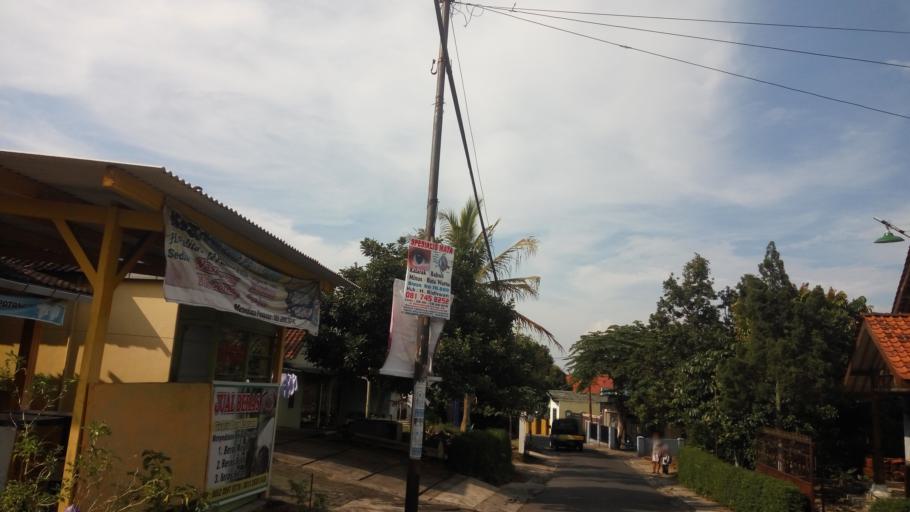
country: ID
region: Central Java
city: Ungaran
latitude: -7.1448
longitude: 110.4116
